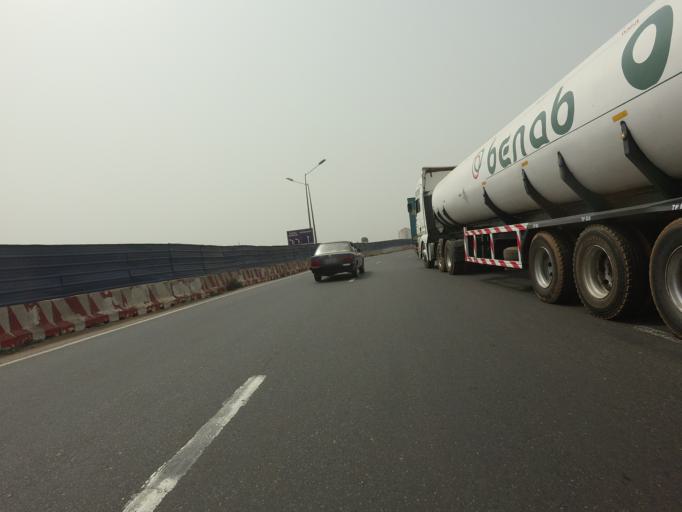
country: GH
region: Greater Accra
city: Tema
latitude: 5.6865
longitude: -0.0131
